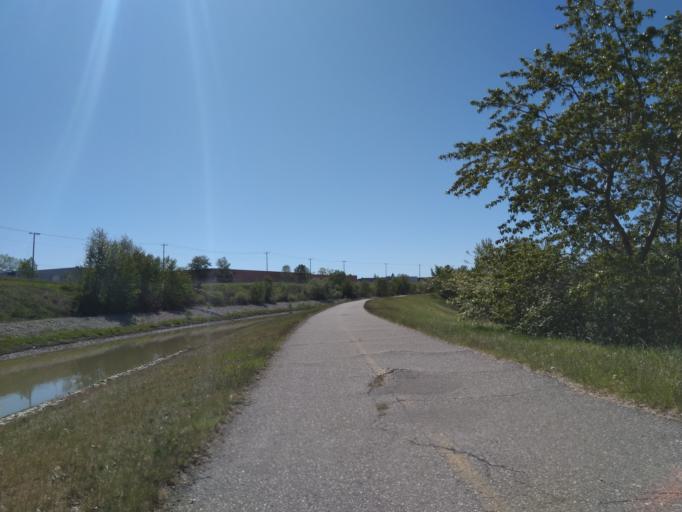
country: CA
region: Alberta
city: Calgary
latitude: 50.9949
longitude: -113.9881
